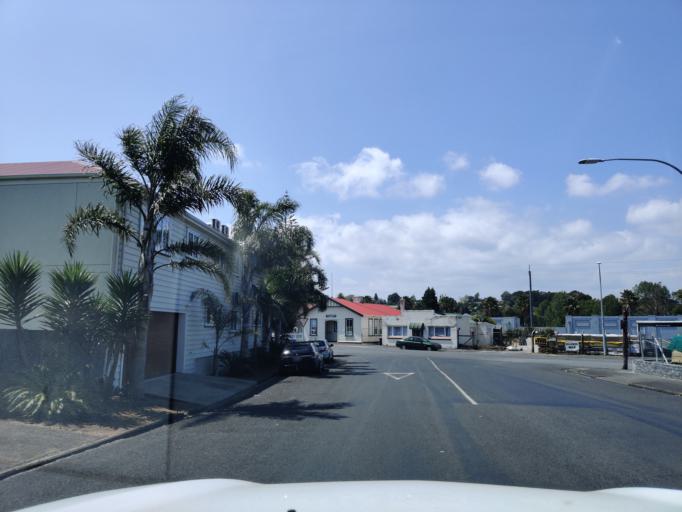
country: NZ
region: Auckland
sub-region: Auckland
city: Pukekohe East
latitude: -37.2581
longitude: 174.9477
